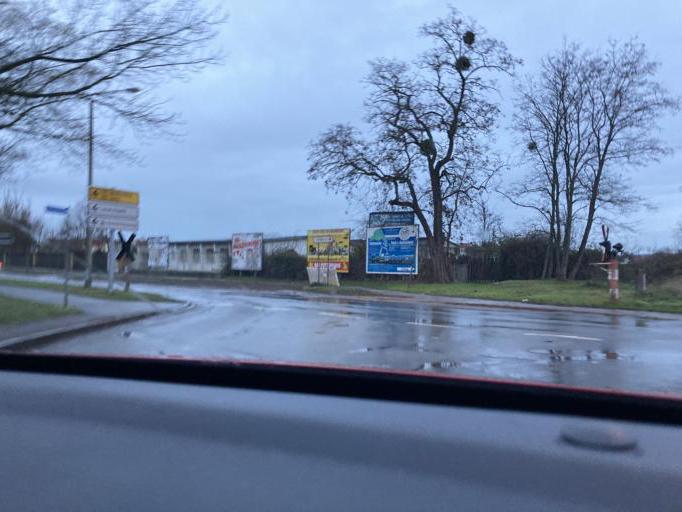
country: DE
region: Saxony-Anhalt
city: Naumburg
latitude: 51.1517
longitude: 11.8255
